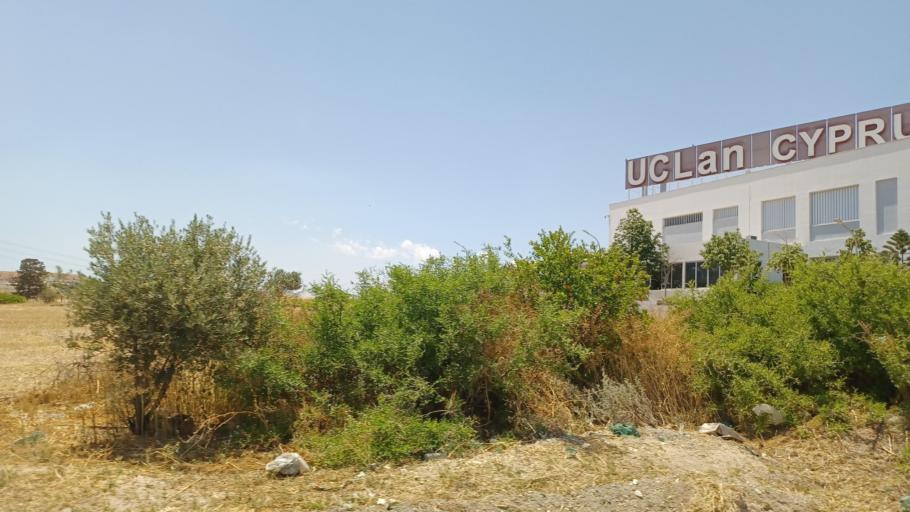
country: CY
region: Larnaka
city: Pyla
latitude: 35.0080
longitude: 33.6980
